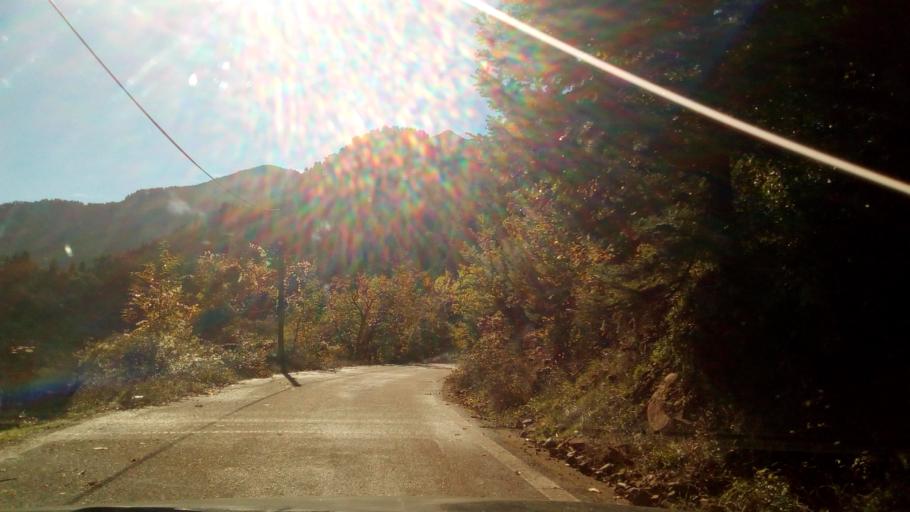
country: GR
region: West Greece
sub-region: Nomos Aitolias kai Akarnanias
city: Nafpaktos
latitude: 38.5884
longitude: 21.8763
